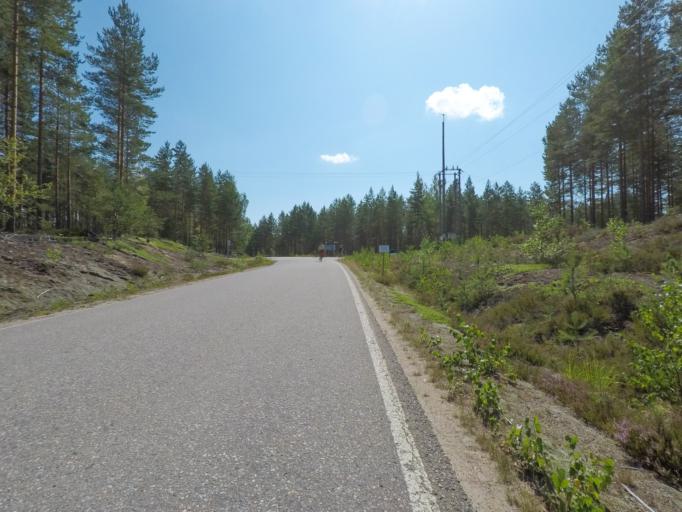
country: FI
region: Southern Savonia
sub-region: Mikkeli
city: Puumala
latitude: 61.4610
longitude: 28.1757
